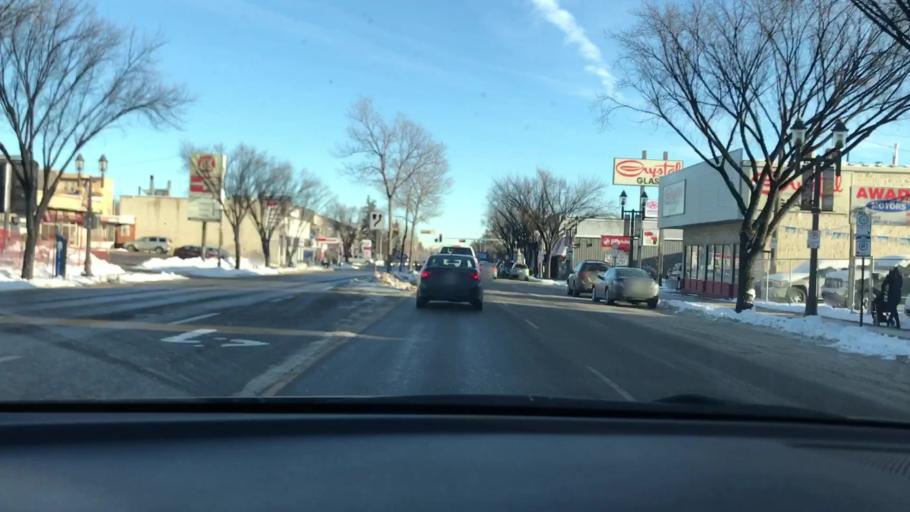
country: CA
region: Alberta
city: Edmonton
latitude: 53.5180
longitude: -113.4885
